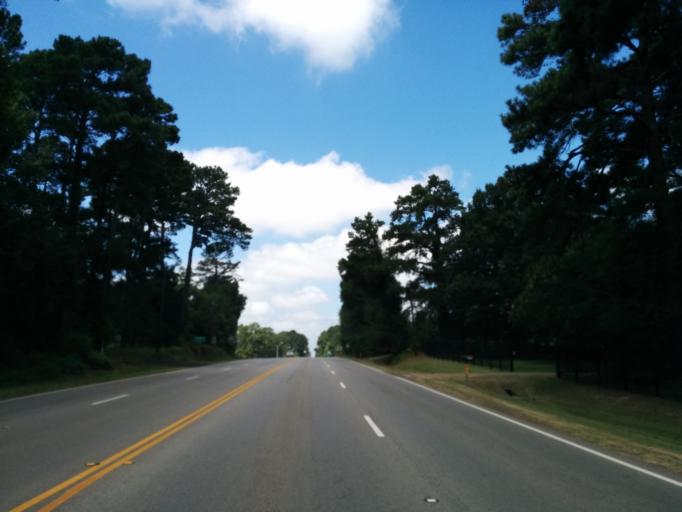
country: US
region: Texas
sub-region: Houston County
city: Crockett
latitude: 31.3108
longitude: -95.4799
